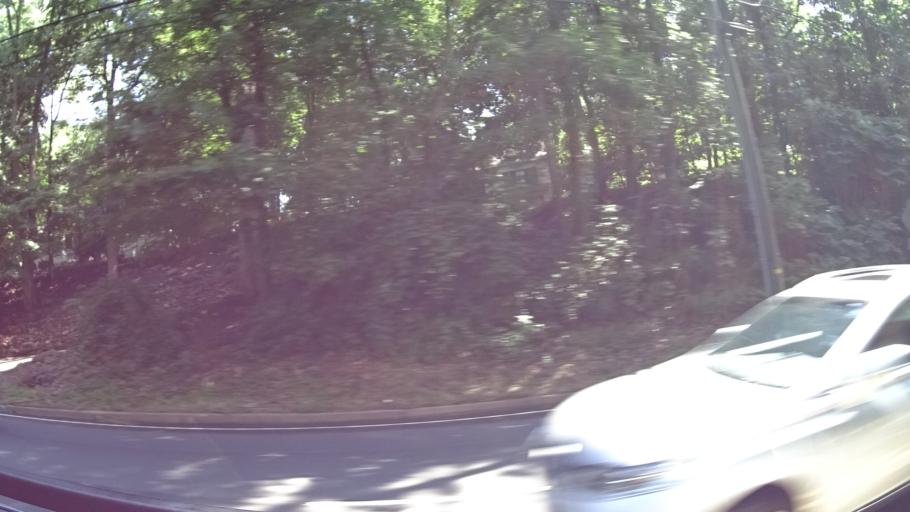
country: US
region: New Jersey
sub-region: Union County
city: New Providence
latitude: 40.6763
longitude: -74.4088
